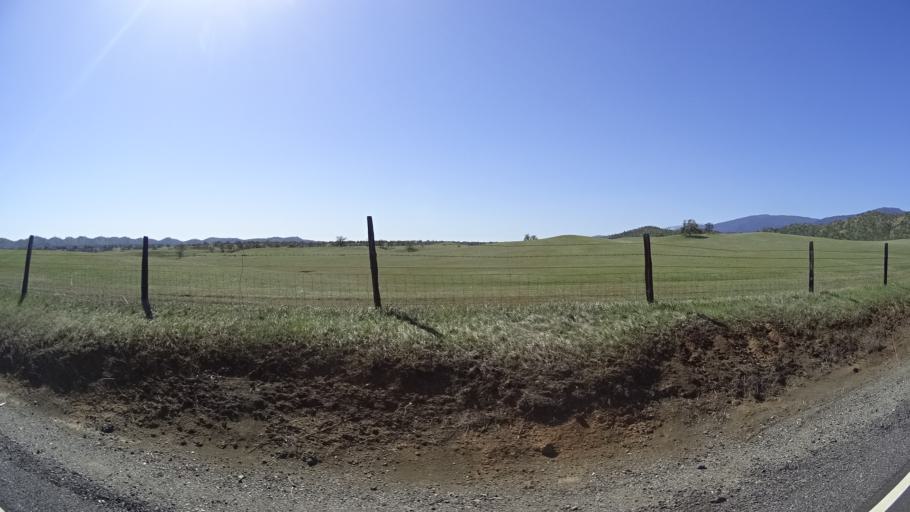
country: US
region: California
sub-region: Glenn County
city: Orland
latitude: 39.6575
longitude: -122.5565
